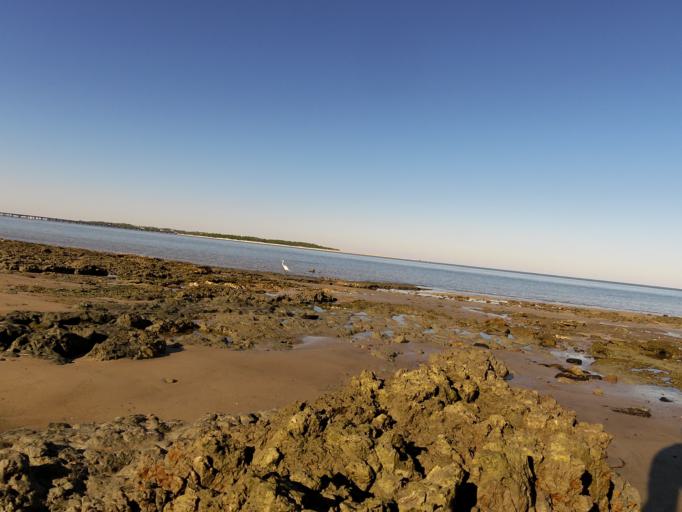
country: US
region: Florida
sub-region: Nassau County
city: Fernandina Beach
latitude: 30.4995
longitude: -81.4448
